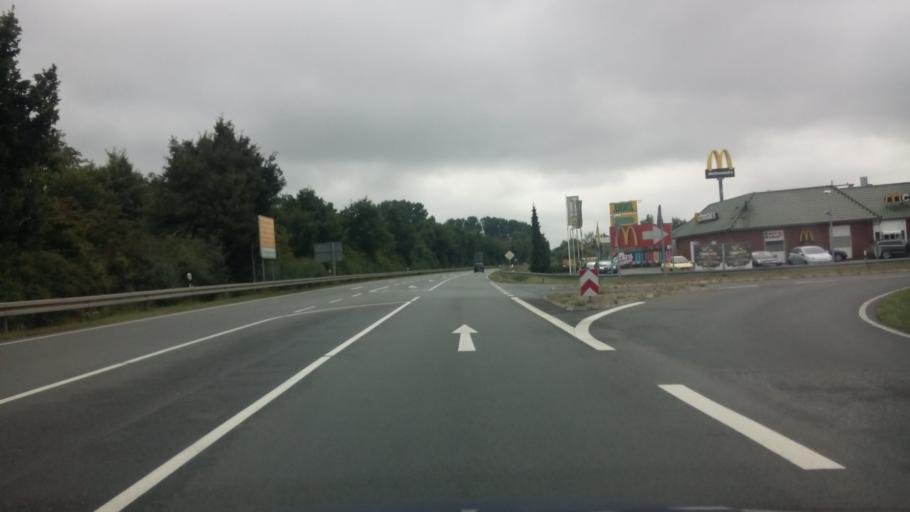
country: DE
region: Lower Saxony
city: Bassum
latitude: 52.8609
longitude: 8.7482
